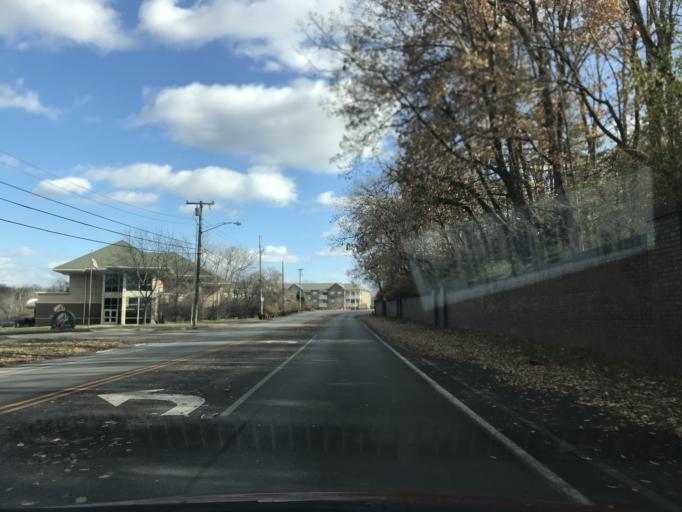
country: US
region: Indiana
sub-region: Clark County
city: Jeffersonville
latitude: 38.2479
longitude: -85.7095
